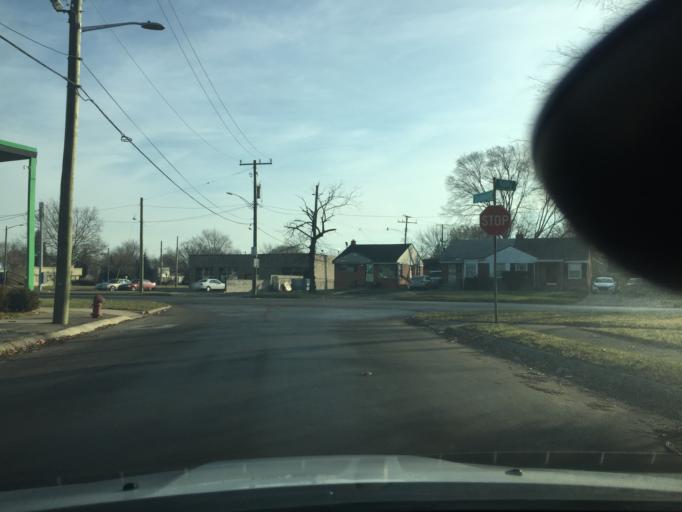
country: US
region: Michigan
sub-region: Wayne County
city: Harper Woods
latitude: 42.4340
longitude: -82.9539
